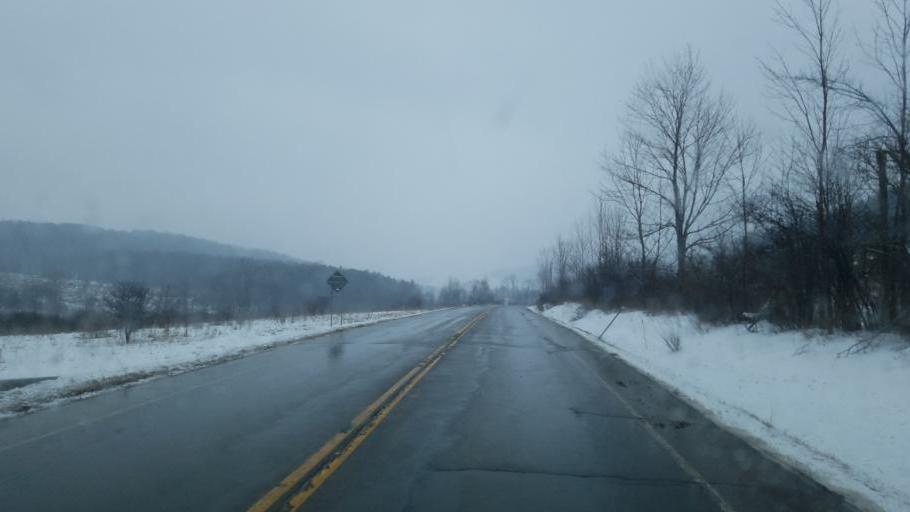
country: US
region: New York
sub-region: Steuben County
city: Canisteo
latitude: 42.1204
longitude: -77.5498
